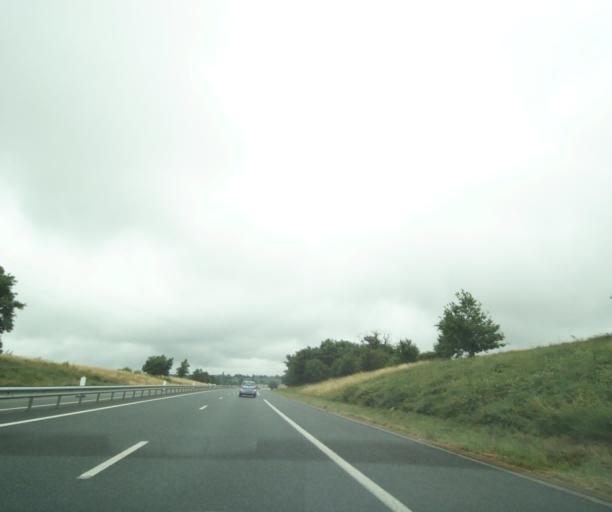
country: FR
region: Midi-Pyrenees
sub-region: Departement de l'Aveyron
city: Luc-la-Primaube
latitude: 44.2982
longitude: 2.5239
